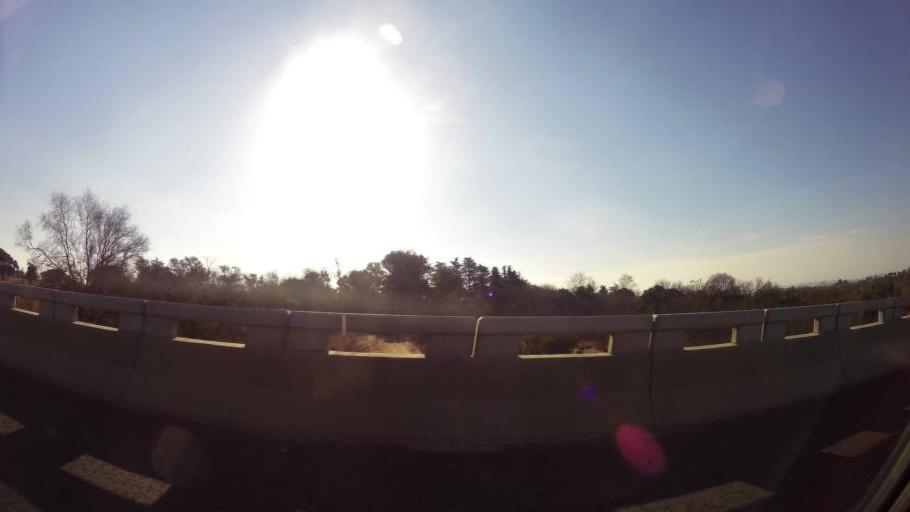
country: ZA
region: Gauteng
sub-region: West Rand District Municipality
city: Muldersdriseloop
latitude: -25.9864
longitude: 27.9206
